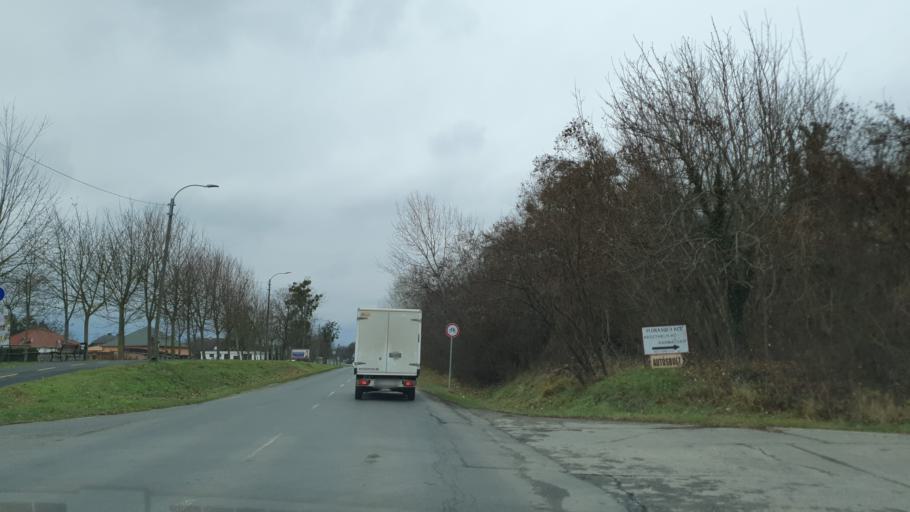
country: HU
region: Zala
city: Keszthely
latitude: 46.7675
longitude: 17.2314
